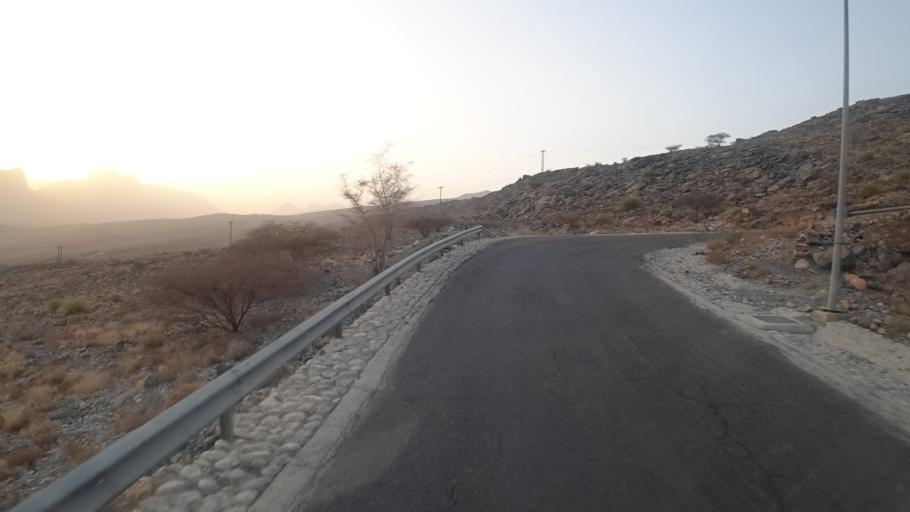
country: OM
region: Muhafazat ad Dakhiliyah
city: Bahla'
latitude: 23.1311
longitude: 57.3034
